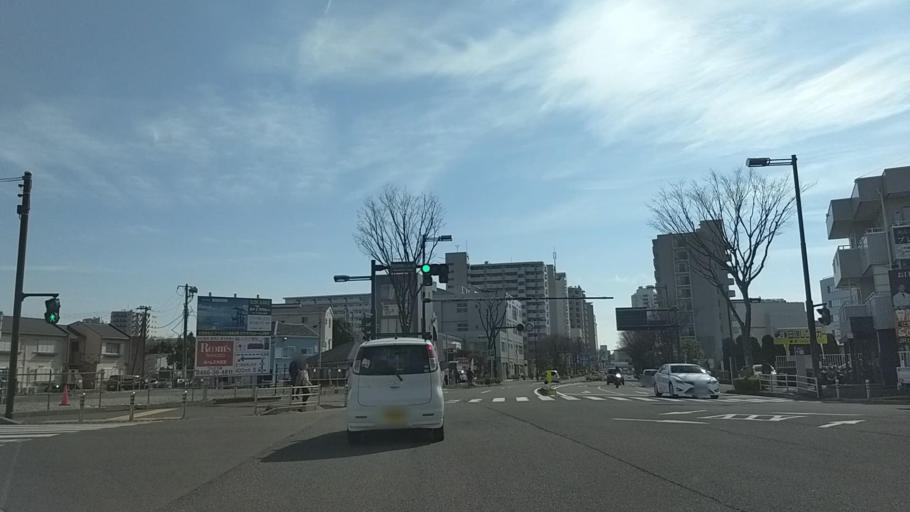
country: JP
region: Kanagawa
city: Fujisawa
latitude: 35.3415
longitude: 139.4492
